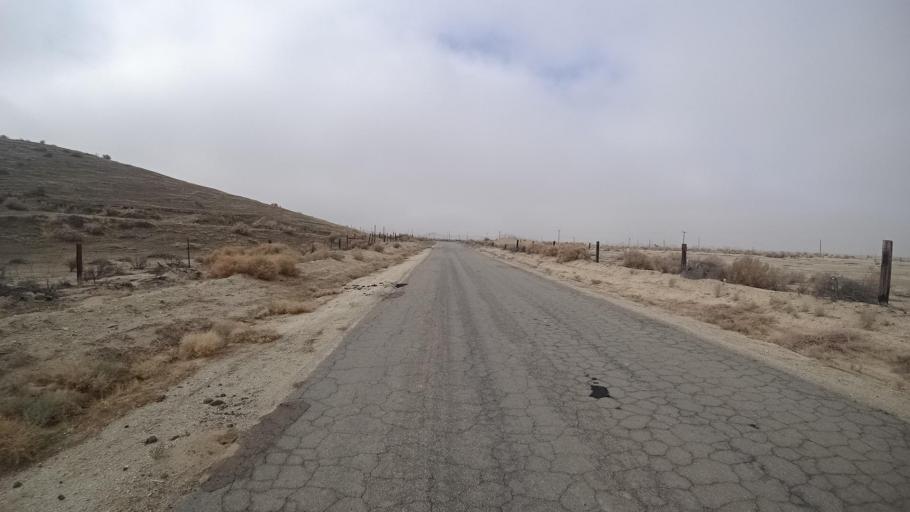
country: US
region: California
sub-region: Kern County
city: Maricopa
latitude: 35.0386
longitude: -119.3805
